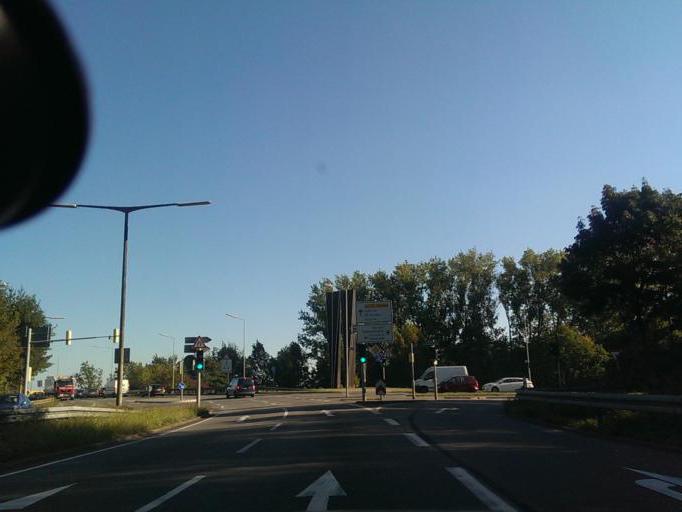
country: DE
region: Baden-Wuerttemberg
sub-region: Karlsruhe Region
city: Karlsruhe
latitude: 48.9969
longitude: 8.4301
